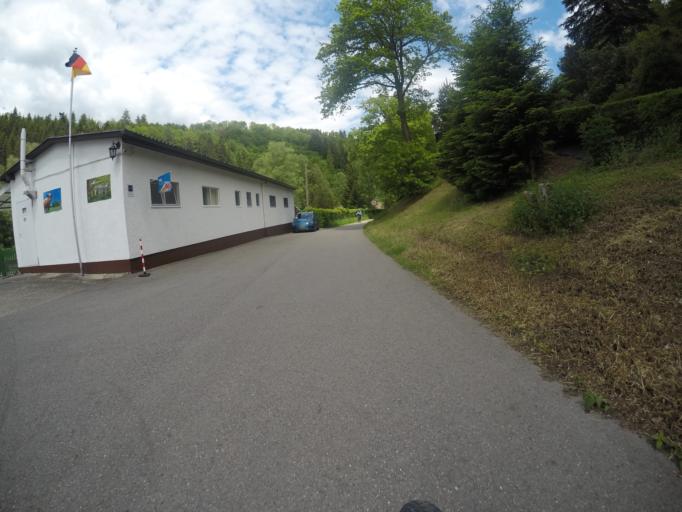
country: DE
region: Baden-Wuerttemberg
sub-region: Karlsruhe Region
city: Wildberg
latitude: 48.6113
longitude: 8.7355
